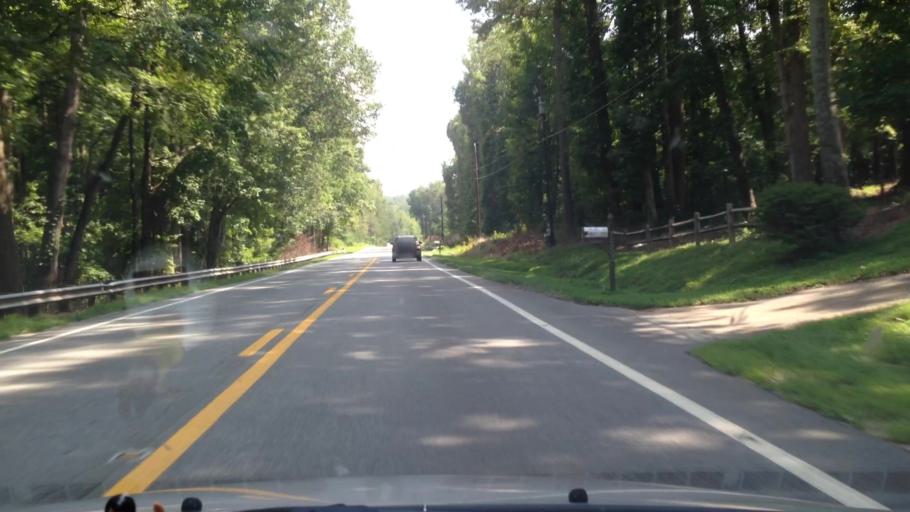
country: US
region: North Carolina
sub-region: Guilford County
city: Oak Ridge
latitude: 36.2057
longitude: -79.9873
